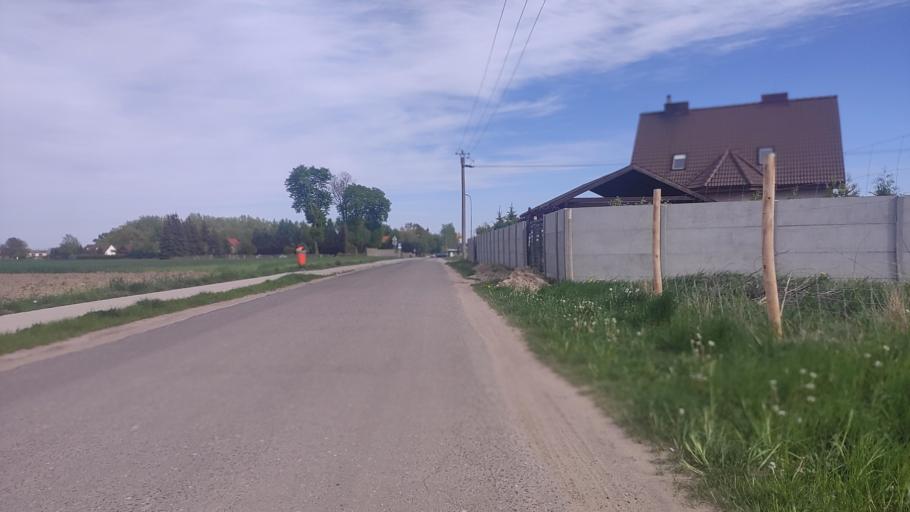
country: PL
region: Greater Poland Voivodeship
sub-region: Powiat poznanski
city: Kleszczewo
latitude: 52.3834
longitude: 17.1554
